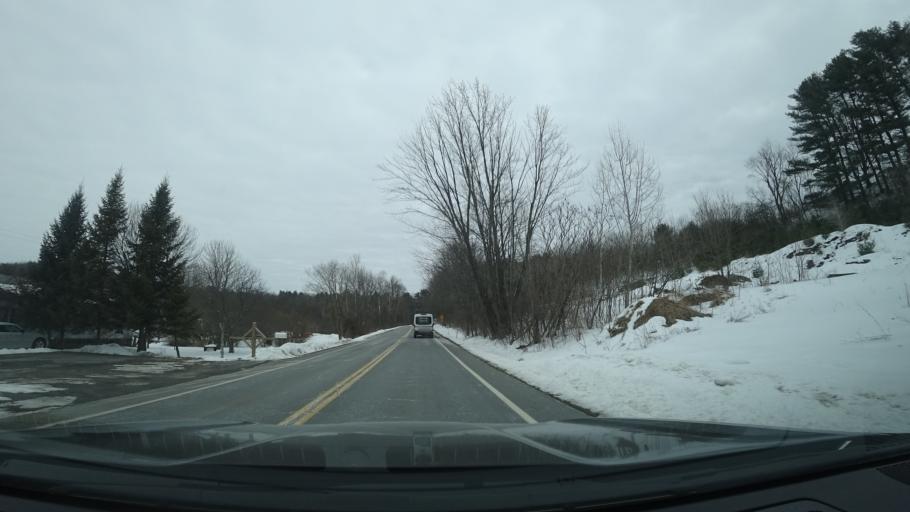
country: US
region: New York
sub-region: Washington County
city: Greenwich
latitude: 43.1890
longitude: -73.4655
